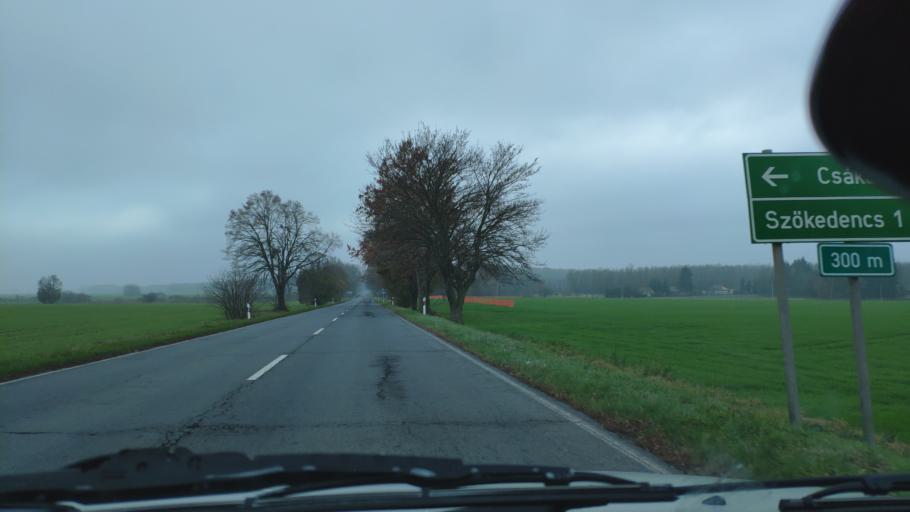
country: HU
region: Zala
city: Zalakomar
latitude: 46.5539
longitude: 17.2569
